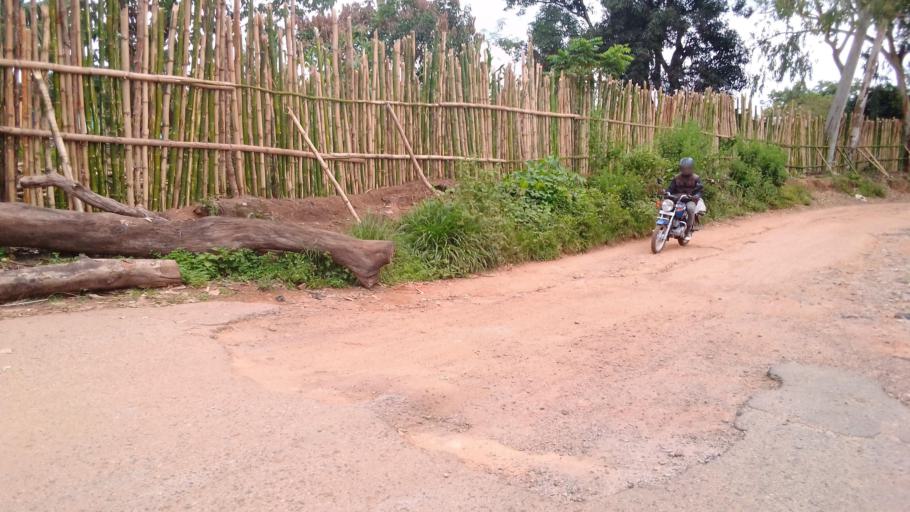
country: SL
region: Northern Province
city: Makeni
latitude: 8.8736
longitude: -12.0325
